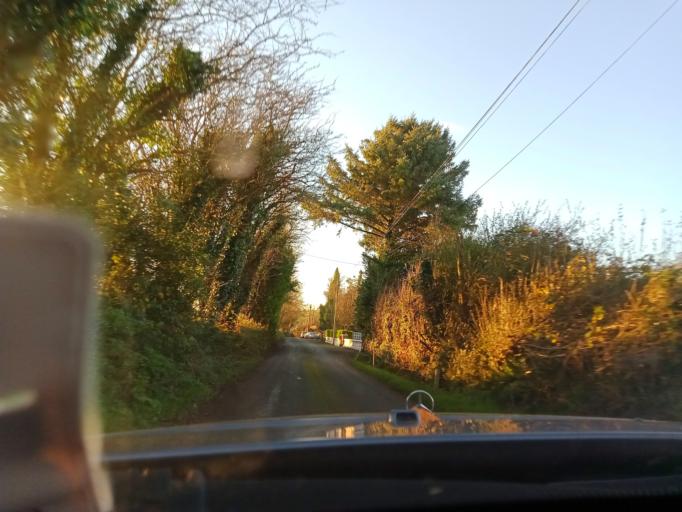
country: IE
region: Leinster
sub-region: Loch Garman
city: New Ross
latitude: 52.3707
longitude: -7.0374
